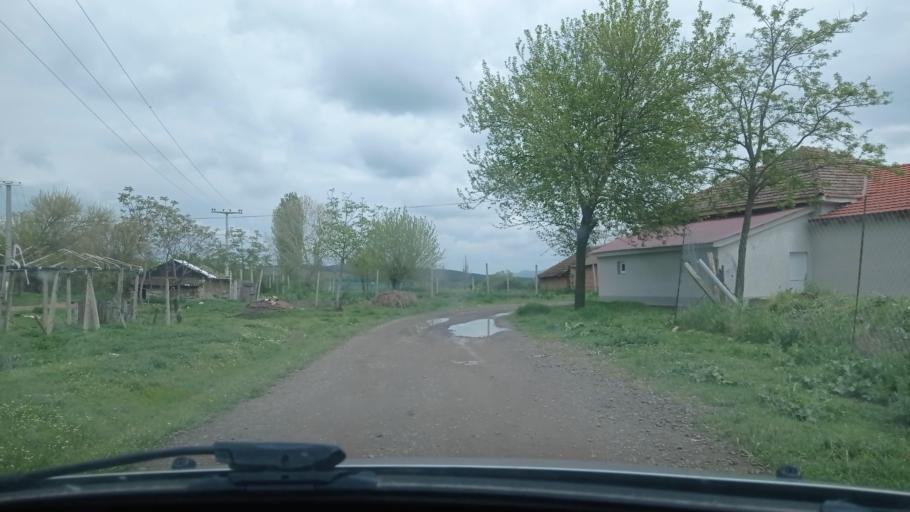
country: MK
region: Lozovo
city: Lozovo
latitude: 41.7665
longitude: 21.8939
